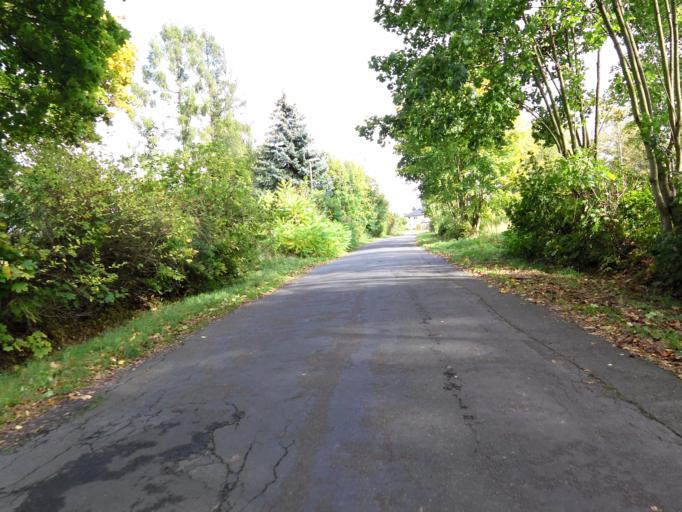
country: DE
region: Saxony
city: Markkleeberg
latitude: 51.2894
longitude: 12.4319
